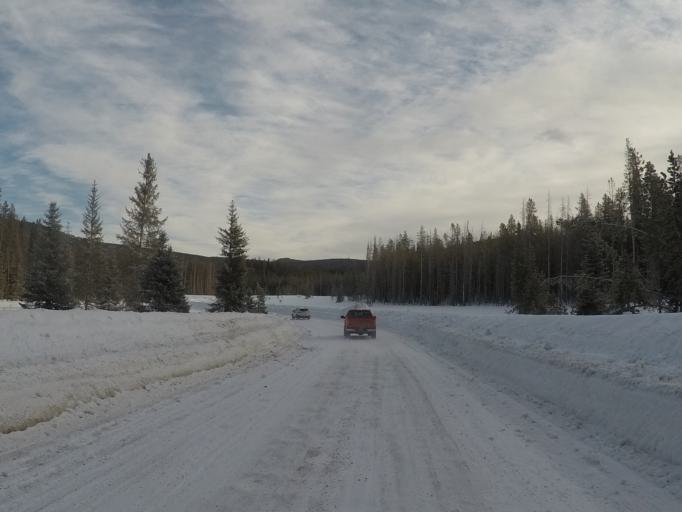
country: US
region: Montana
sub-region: Granite County
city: Philipsburg
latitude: 46.2287
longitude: -113.2489
